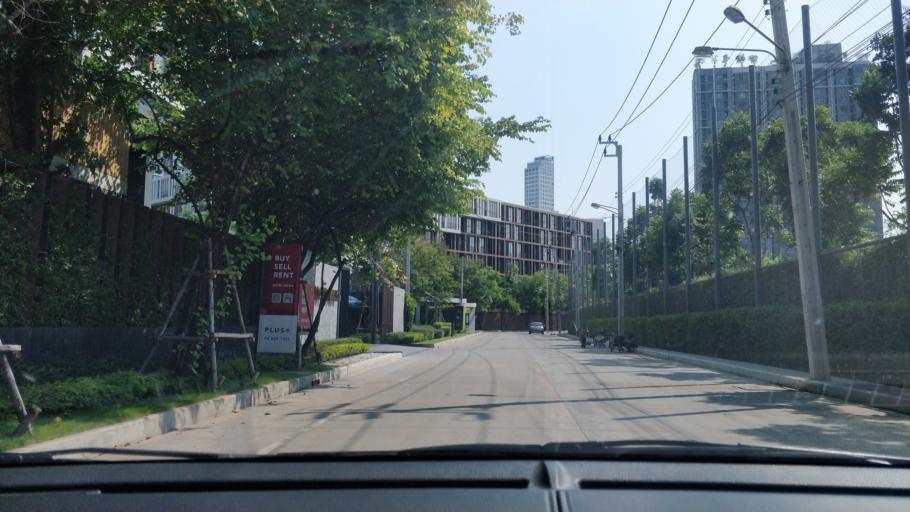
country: TH
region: Bangkok
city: Phra Khanong
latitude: 13.7153
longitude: 100.6024
